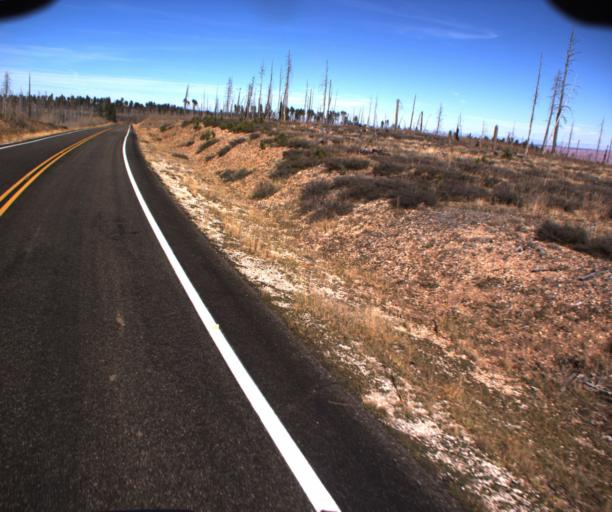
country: US
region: Arizona
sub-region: Coconino County
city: Fredonia
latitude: 36.5902
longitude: -112.1794
